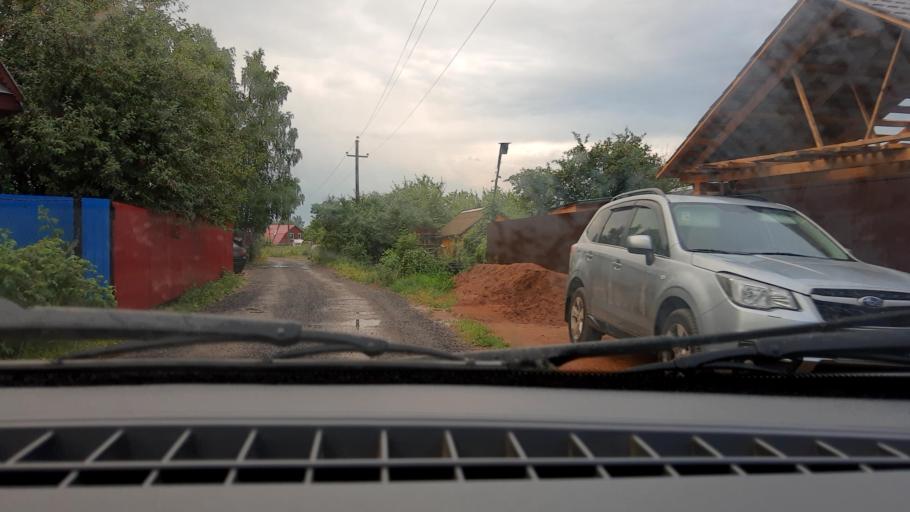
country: RU
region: Bashkortostan
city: Mikhaylovka
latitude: 54.8321
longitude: 55.8313
